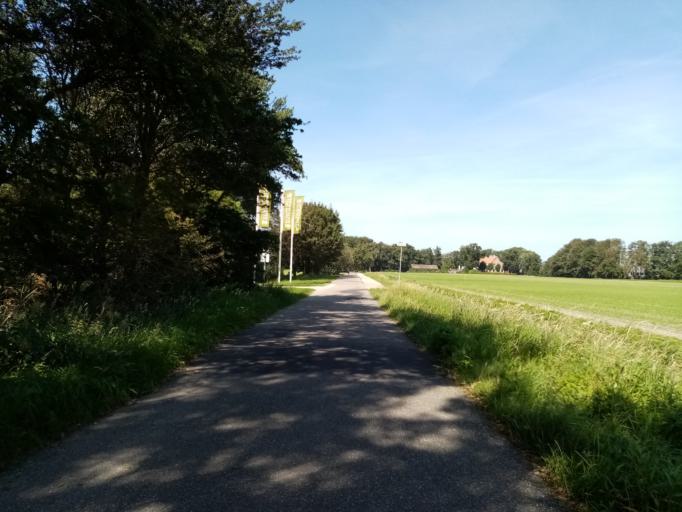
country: NL
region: South Holland
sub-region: Gemeente Lisse
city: Lisse
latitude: 52.2809
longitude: 4.5287
